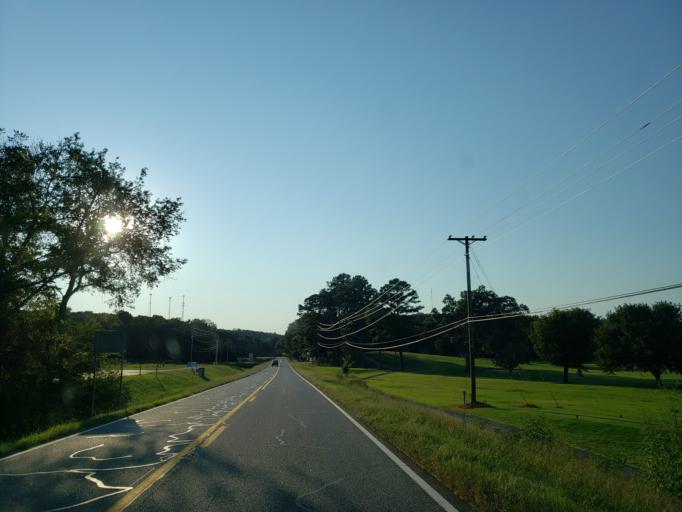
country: US
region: Georgia
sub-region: Gordon County
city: Calhoun
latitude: 34.5421
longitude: -84.9123
